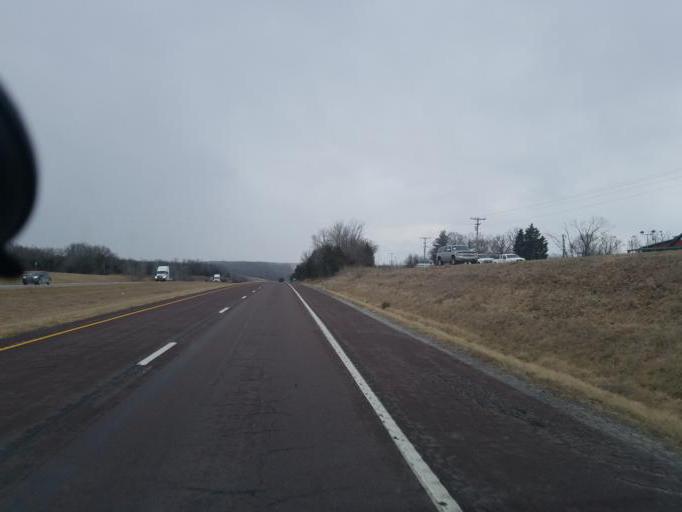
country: US
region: Missouri
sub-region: Boone County
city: Hallsville
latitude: 39.1374
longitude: -92.3326
